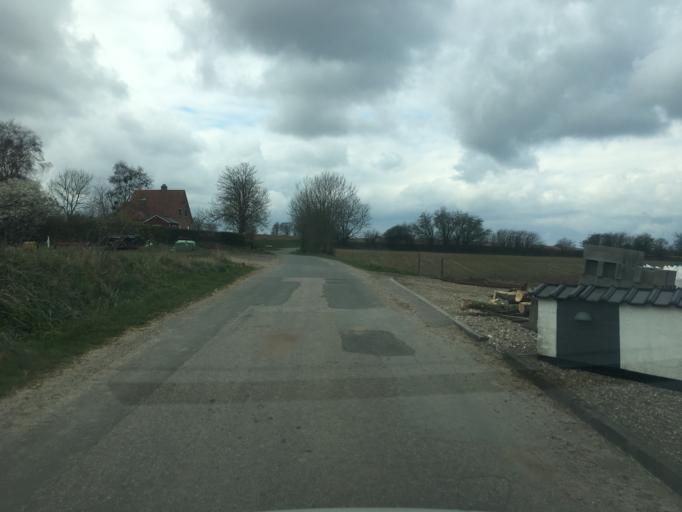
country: DK
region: South Denmark
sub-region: Sonderborg Kommune
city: Grasten
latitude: 55.0051
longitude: 9.5405
